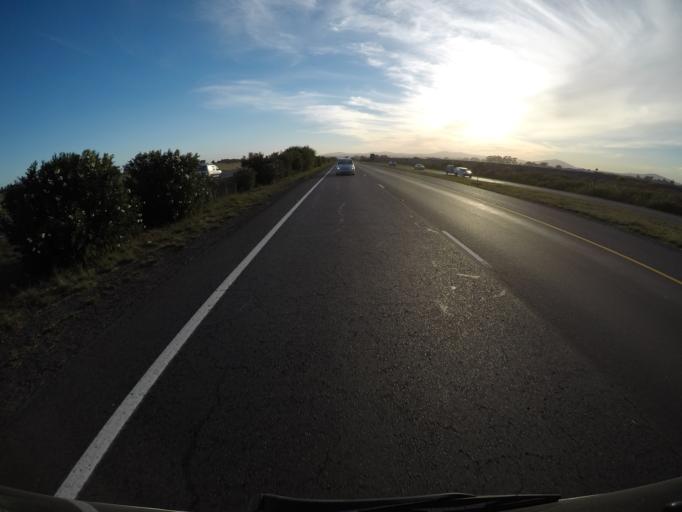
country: ZA
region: Western Cape
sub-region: City of Cape Town
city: Kraaifontein
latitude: -33.8280
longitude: 18.7621
